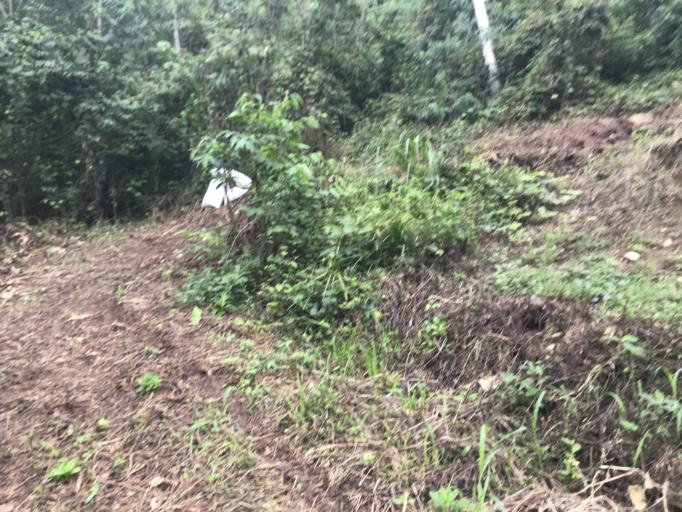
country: PE
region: Pasco
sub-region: Provincia de Oxapampa
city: Villa Rica
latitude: -10.8316
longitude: -75.2928
